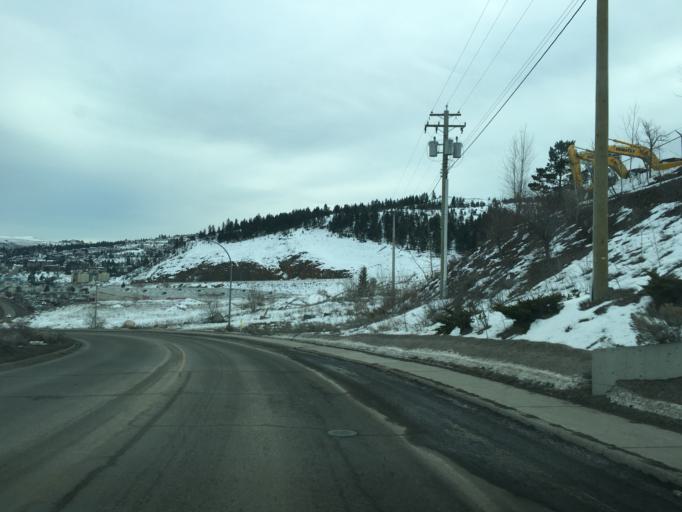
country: CA
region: British Columbia
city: Kamloops
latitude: 50.6572
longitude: -120.3933
